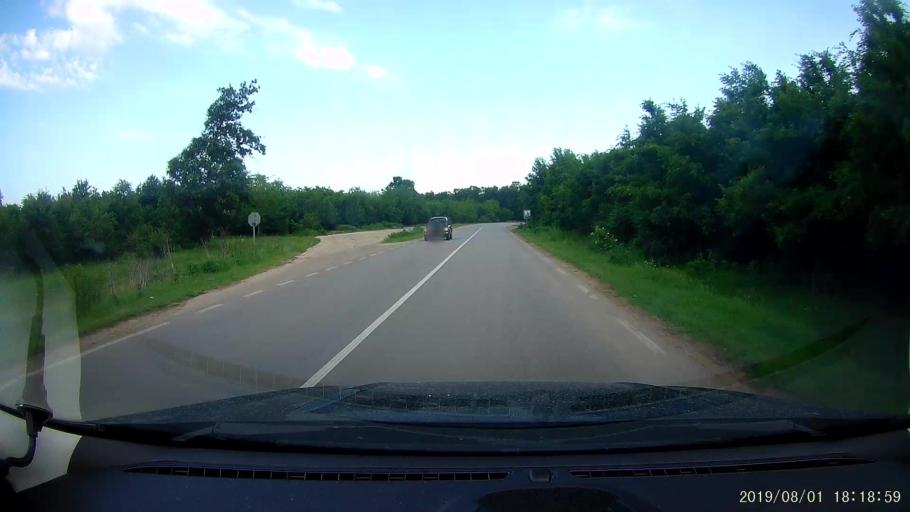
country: BG
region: Shumen
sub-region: Obshtina Kaolinovo
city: Kaolinovo
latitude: 43.6895
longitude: 27.0870
